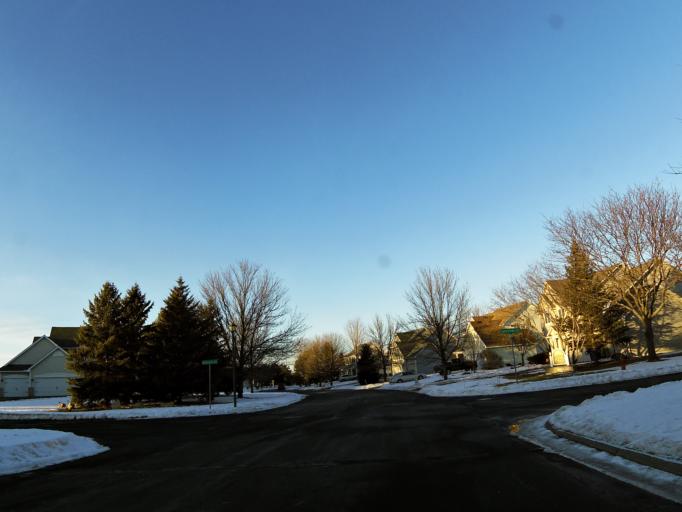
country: US
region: Minnesota
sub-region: Washington County
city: Woodbury
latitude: 44.8916
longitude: -92.8991
